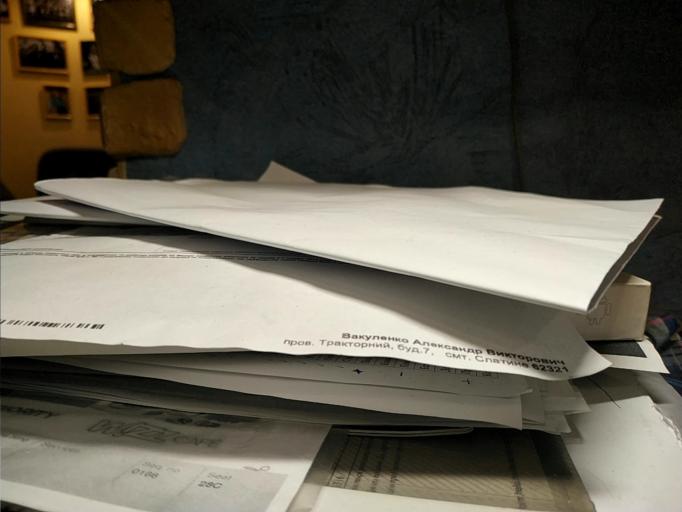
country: RU
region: Tverskaya
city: Zubtsov
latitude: 56.0976
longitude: 34.7029
